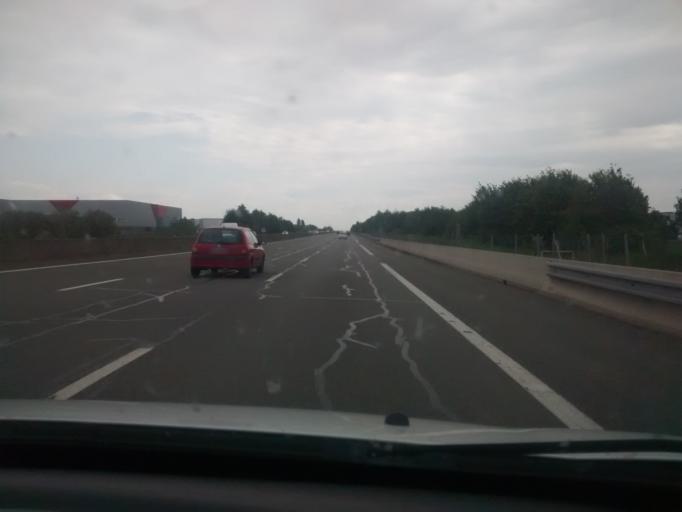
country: FR
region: Centre
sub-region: Departement d'Eure-et-Loir
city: Le Coudray
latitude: 48.4355
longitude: 1.5220
